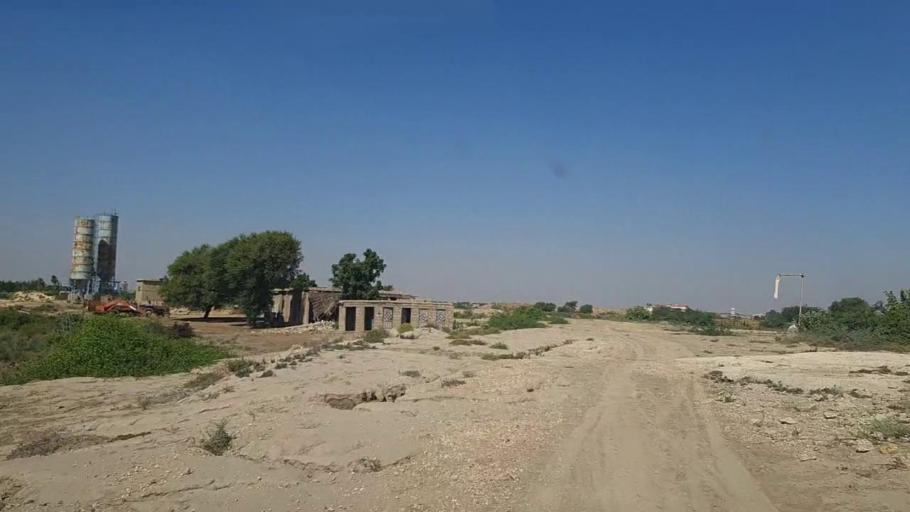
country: PK
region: Sindh
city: Thatta
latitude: 24.8088
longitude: 67.9878
